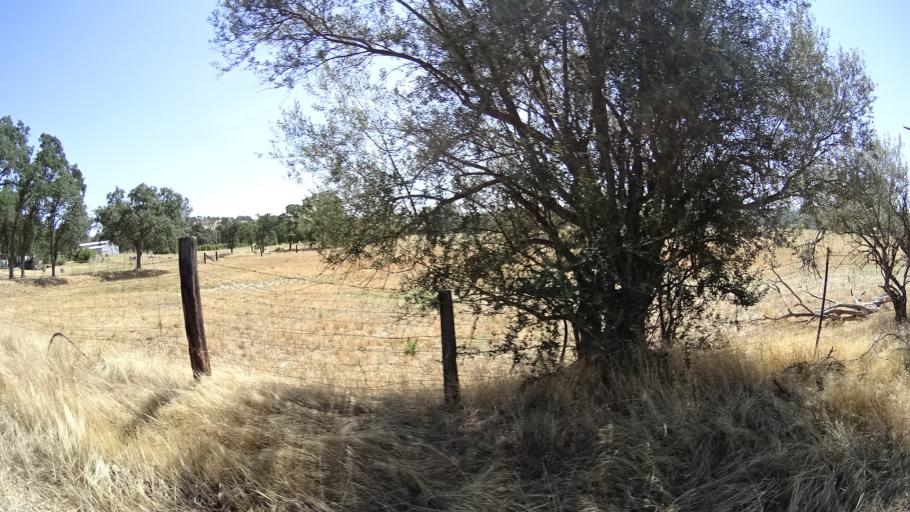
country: US
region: California
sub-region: Calaveras County
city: Rancho Calaveras
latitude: 38.1617
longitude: -120.8955
